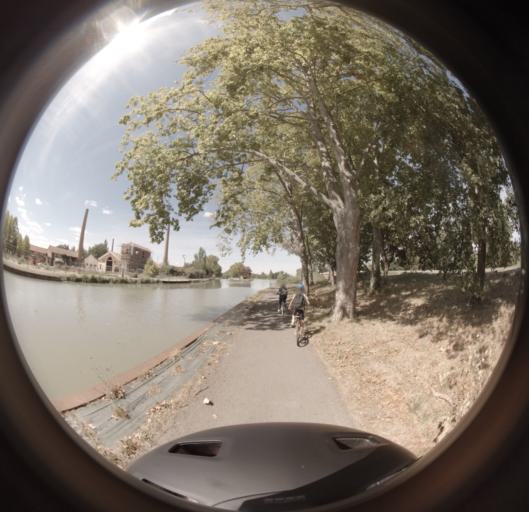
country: FR
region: Midi-Pyrenees
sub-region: Departement du Tarn-et-Garonne
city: Montech
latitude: 43.9623
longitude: 1.2361
